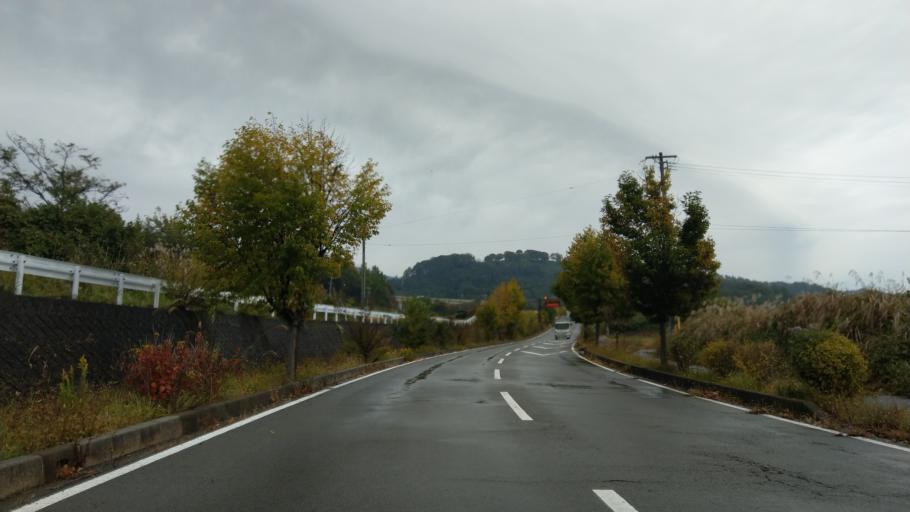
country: JP
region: Nagano
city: Komoro
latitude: 36.3433
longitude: 138.4060
